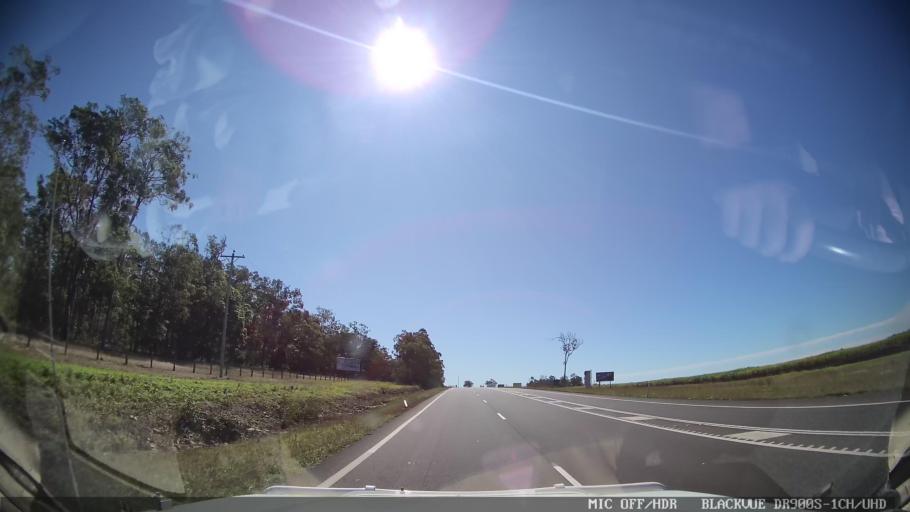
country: AU
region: Queensland
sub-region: Fraser Coast
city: Maryborough
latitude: -25.6432
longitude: 152.6382
